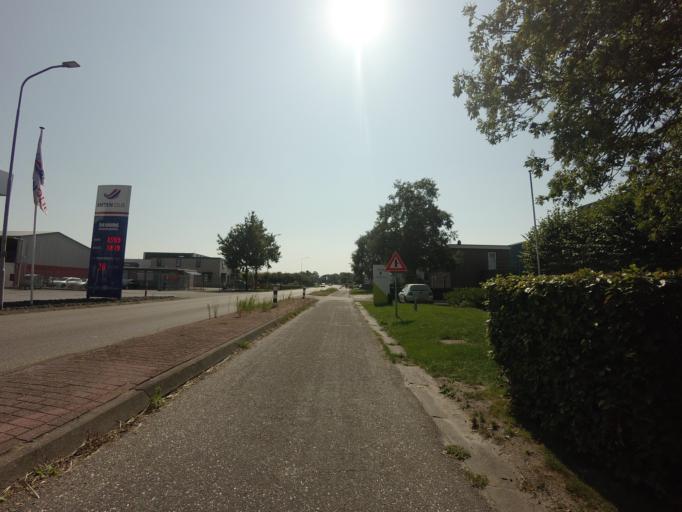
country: NL
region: Groningen
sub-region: Gemeente Zuidhorn
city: Grijpskerk
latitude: 53.2673
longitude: 6.3068
